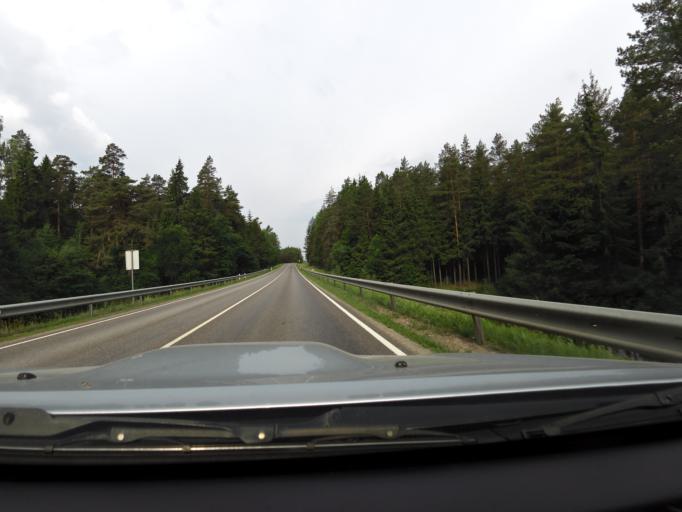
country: LT
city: Aukstadvaris
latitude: 54.5904
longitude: 24.6906
